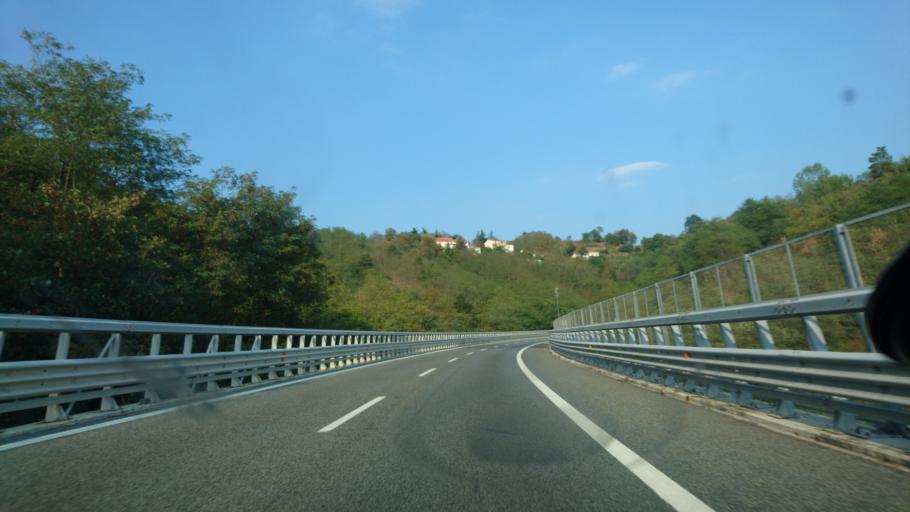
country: IT
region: Liguria
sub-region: Provincia di Savona
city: Altare
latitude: 44.3337
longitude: 8.3688
